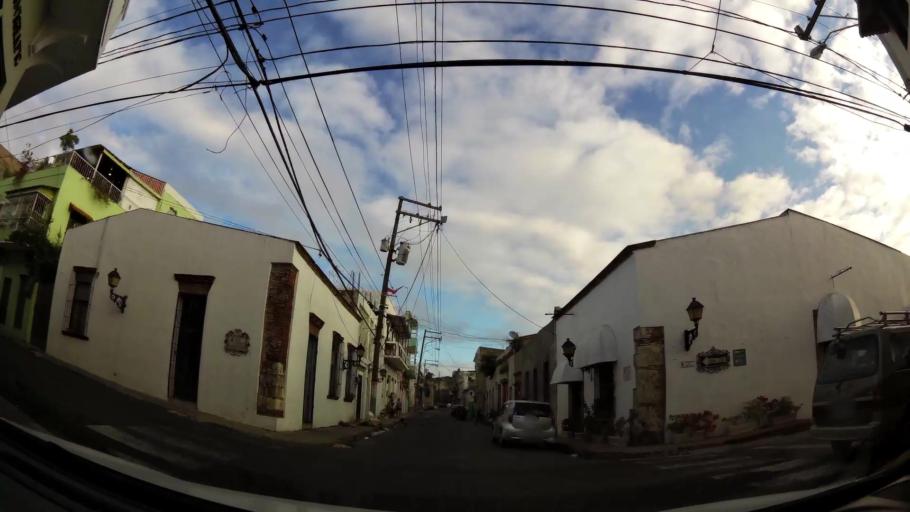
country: DO
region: Nacional
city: San Carlos
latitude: 18.4780
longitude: -69.8843
